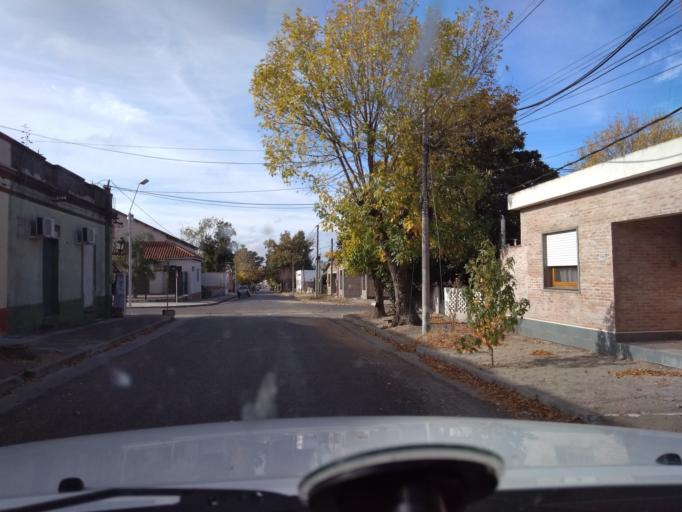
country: UY
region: Florida
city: Florida
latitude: -34.1051
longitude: -56.2134
